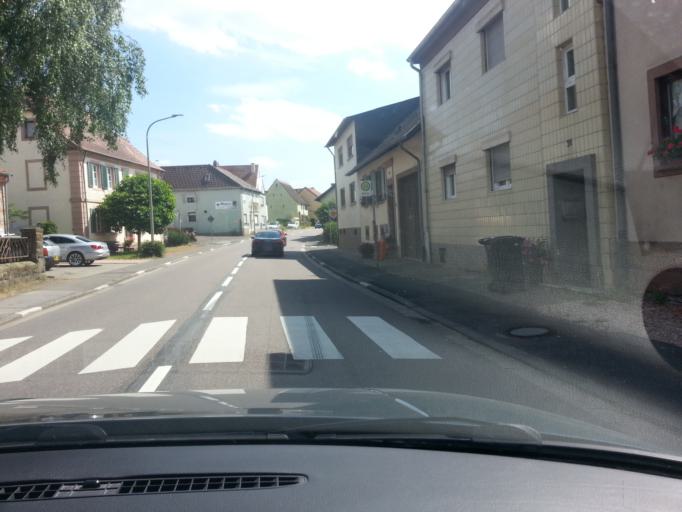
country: DE
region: Saarland
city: Blieskastel
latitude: 49.2291
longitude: 7.2672
